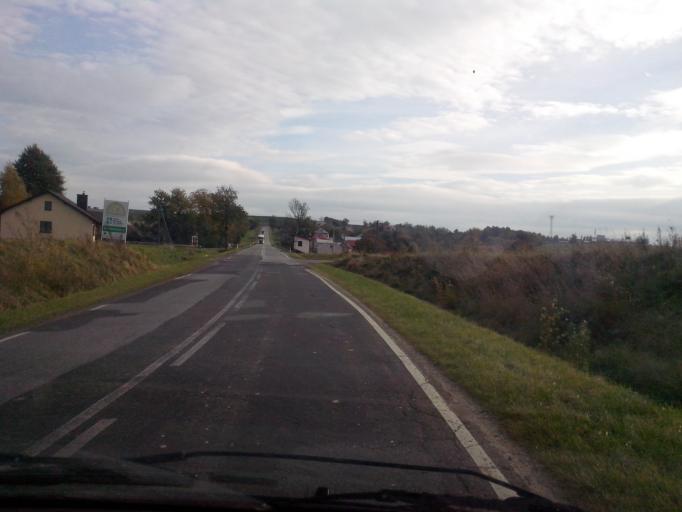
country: PL
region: Subcarpathian Voivodeship
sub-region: Powiat ropczycko-sedziszowski
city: Wielopole Skrzynskie
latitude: 49.9231
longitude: 21.6102
